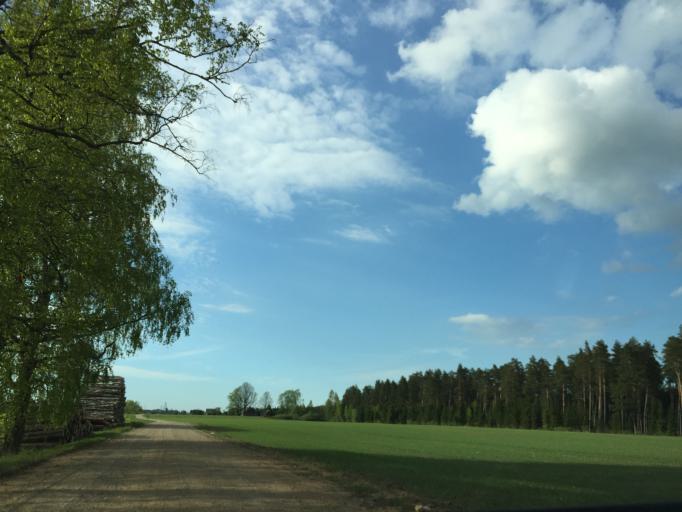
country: LV
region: Limbazu Rajons
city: Limbazi
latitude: 57.3577
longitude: 24.6991
